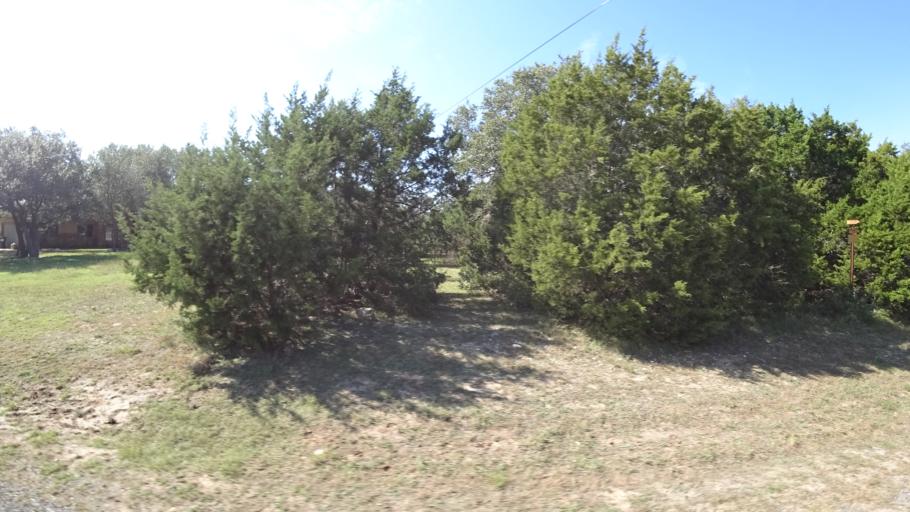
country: US
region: Texas
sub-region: Travis County
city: Bee Cave
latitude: 30.2245
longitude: -97.9359
